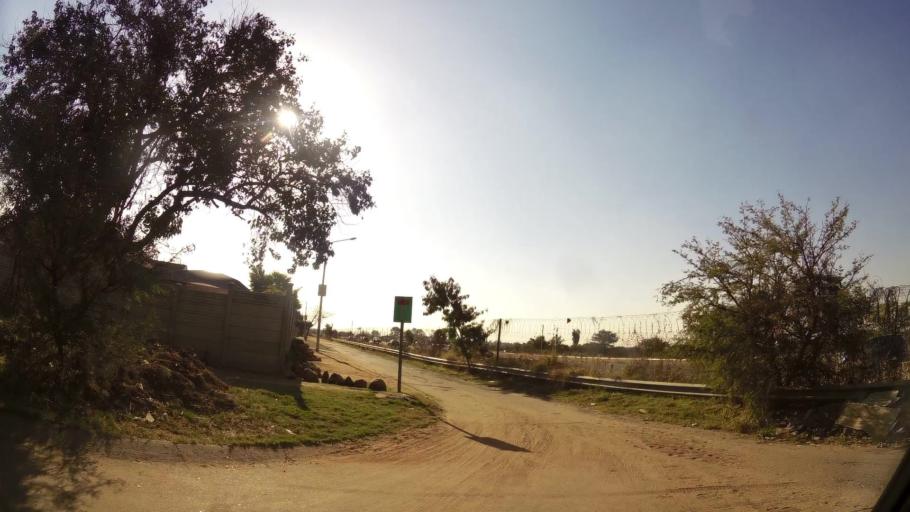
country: ZA
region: North-West
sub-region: Bojanala Platinum District Municipality
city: Rustenburg
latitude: -25.6537
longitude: 27.2610
